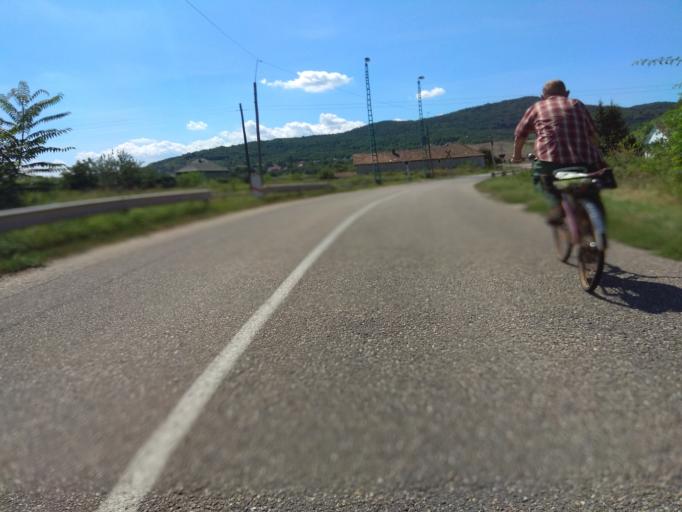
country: HU
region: Borsod-Abauj-Zemplen
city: Sajokaza
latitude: 48.2737
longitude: 20.5794
